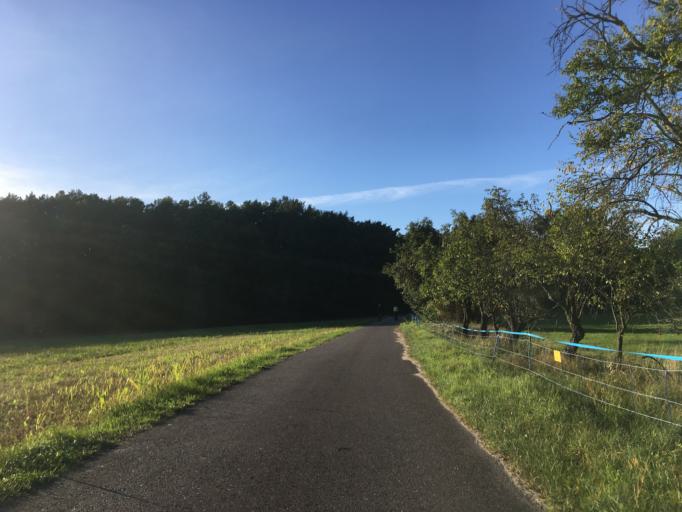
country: PL
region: Lubusz
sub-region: Powiat zarski
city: Trzebiel
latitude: 51.6241
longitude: 14.7560
